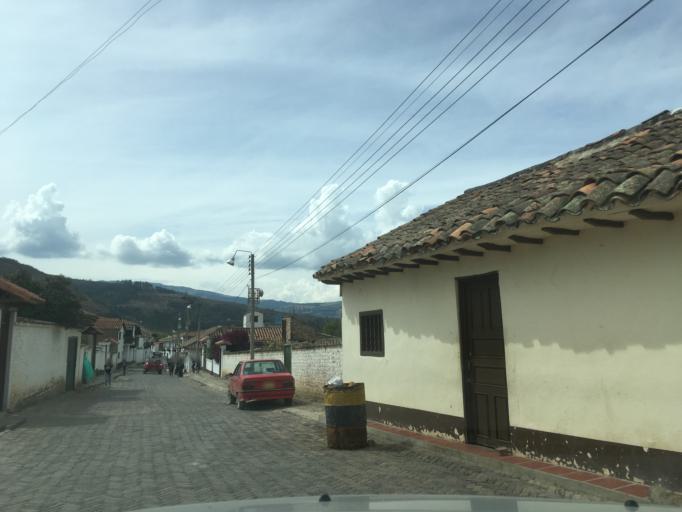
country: CO
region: Boyaca
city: Firavitoba
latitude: 5.6129
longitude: -72.9780
